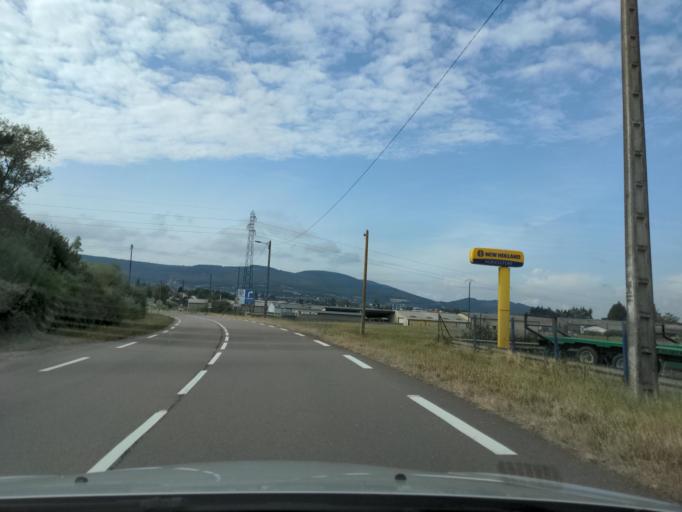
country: FR
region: Bourgogne
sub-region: Departement de Saone-et-Loire
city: Autun
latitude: 46.9751
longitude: 4.3071
